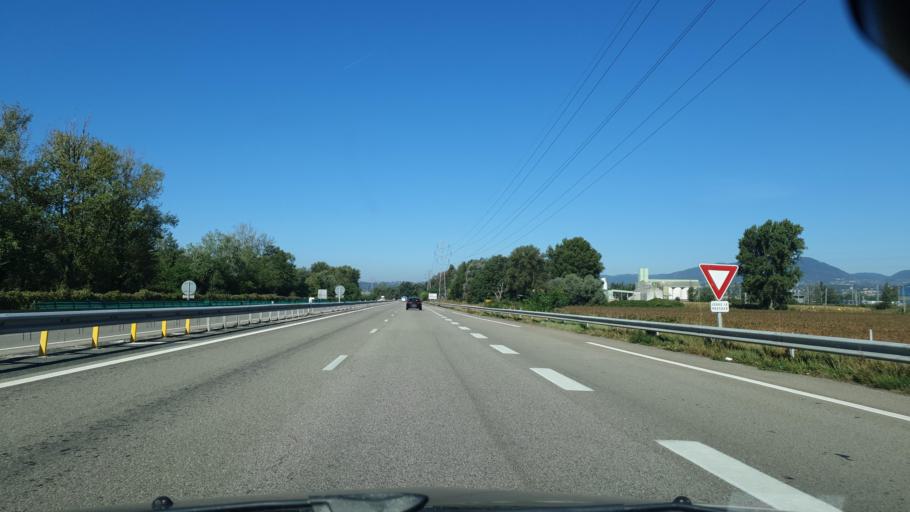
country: FR
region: Rhone-Alpes
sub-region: Departement de l'Isere
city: Voreppe
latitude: 45.3002
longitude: 5.6167
